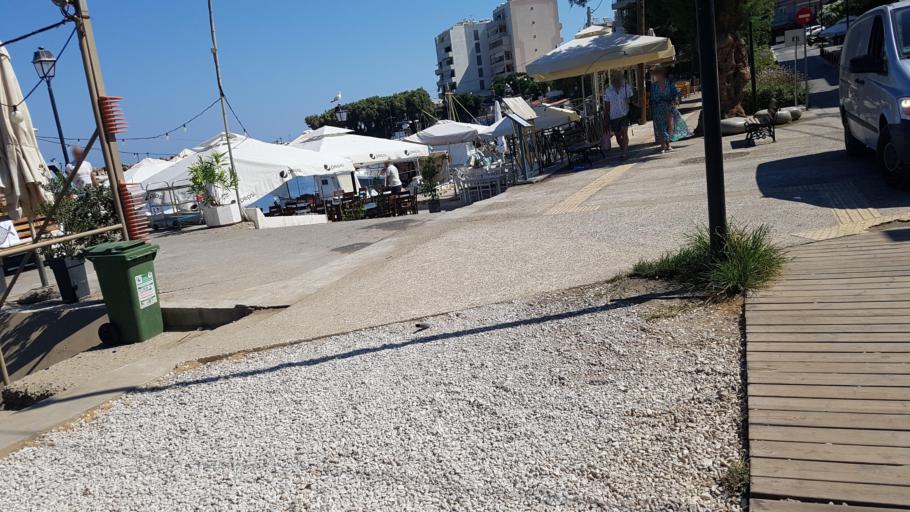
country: GR
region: Crete
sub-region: Nomos Chanias
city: Chania
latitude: 35.5149
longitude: 24.0082
